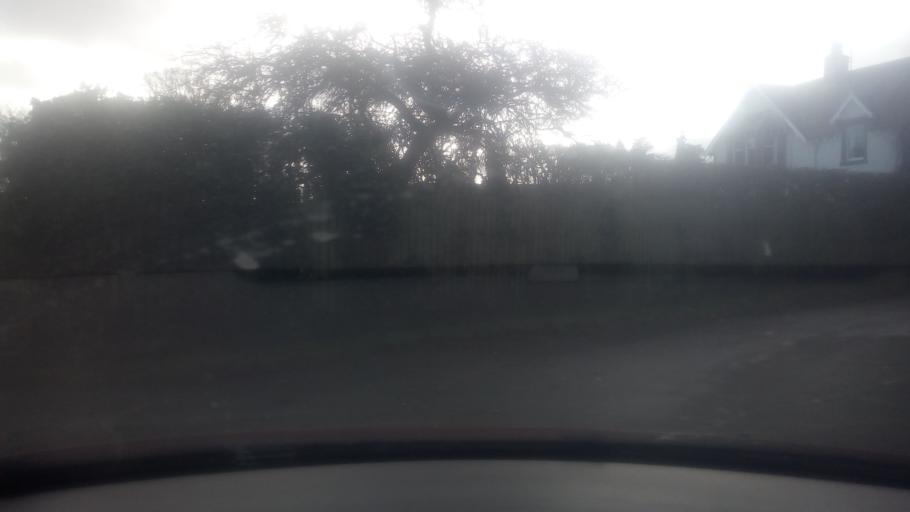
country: GB
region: Scotland
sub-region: The Scottish Borders
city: Saint Boswells
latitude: 55.5210
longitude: -2.6520
